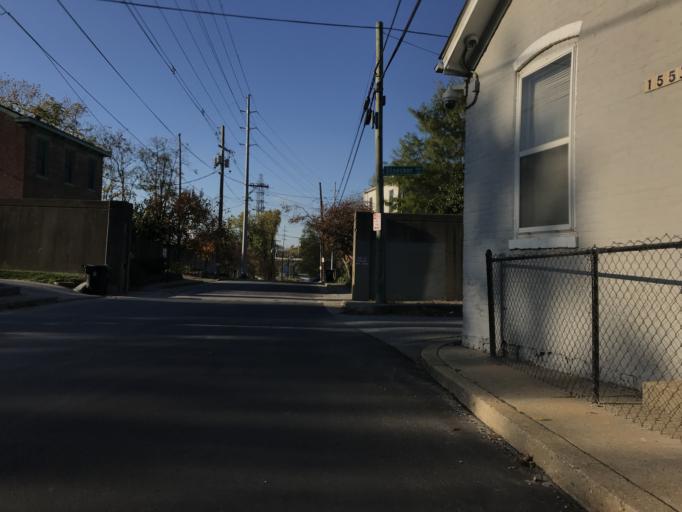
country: US
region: Indiana
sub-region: Clark County
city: Jeffersonville
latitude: 38.2593
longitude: -85.7218
